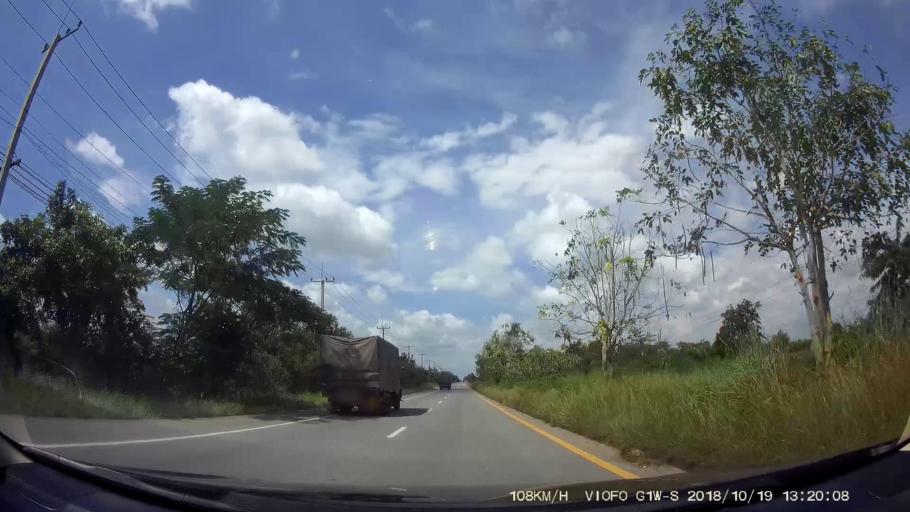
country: TH
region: Chaiyaphum
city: Chatturat
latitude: 15.4409
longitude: 101.8293
